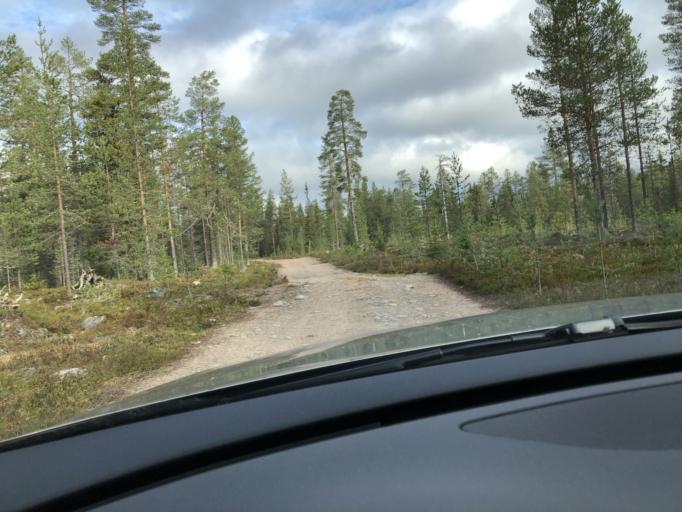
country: FI
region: Lapland
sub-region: Itae-Lappi
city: Posio
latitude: 66.0604
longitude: 27.8120
